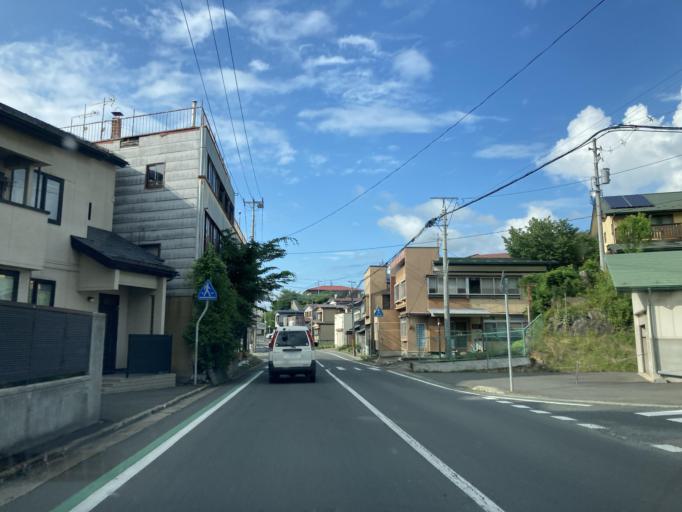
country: JP
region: Iwate
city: Ichinohe
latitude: 39.9663
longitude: 141.2211
